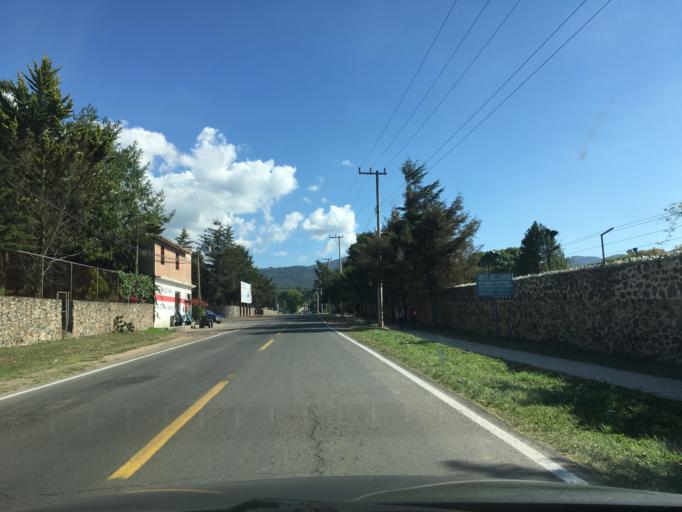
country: MX
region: Hidalgo
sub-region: Omitlan de Juarez
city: San Antonio el Paso
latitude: 20.2109
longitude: -98.5678
